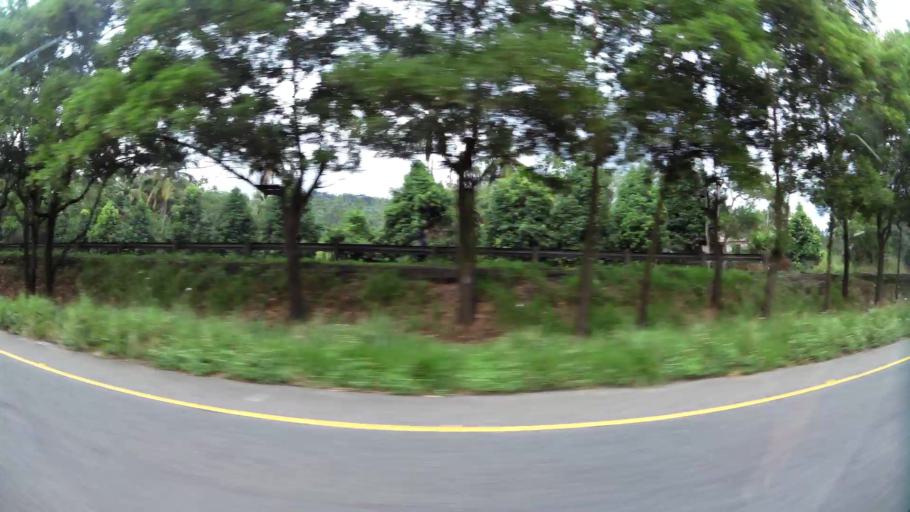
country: DO
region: Monsenor Nouel
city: Piedra Blanca
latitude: 18.7901
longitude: -70.2694
